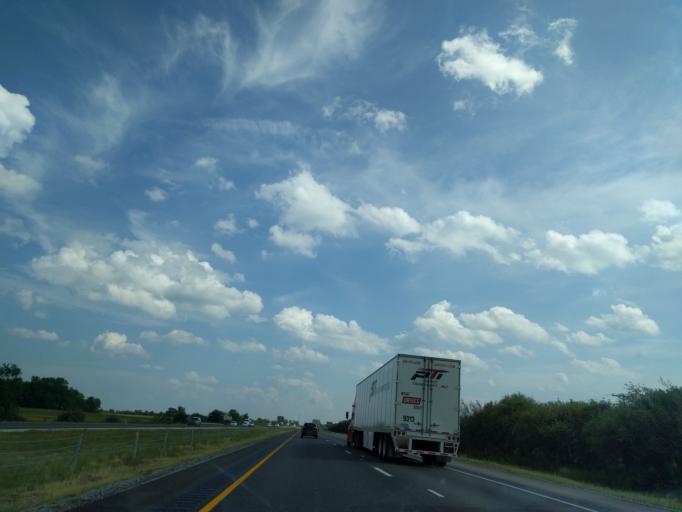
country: US
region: Indiana
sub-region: Jasper County
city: Remington
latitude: 40.7934
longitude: -87.1384
